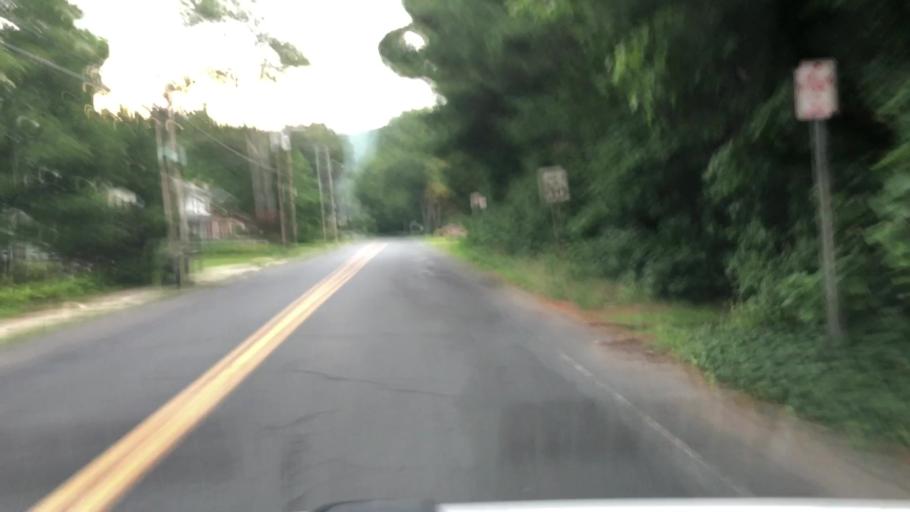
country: US
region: Massachusetts
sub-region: Hampshire County
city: Easthampton
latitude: 42.2702
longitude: -72.6492
